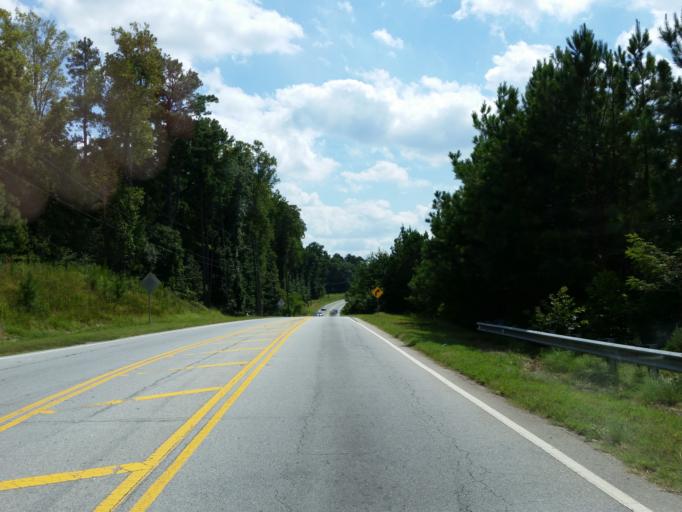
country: US
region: Georgia
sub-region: Gwinnett County
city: Lawrenceville
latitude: 33.9755
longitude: -83.9457
